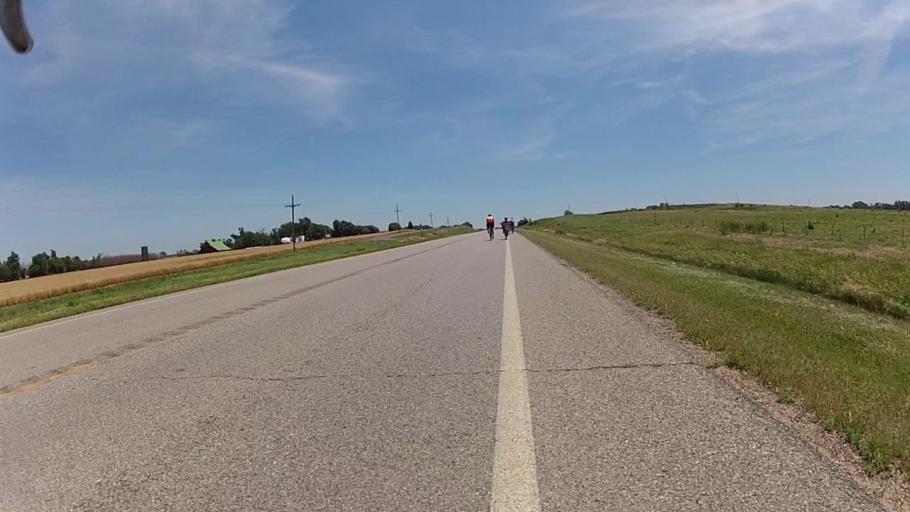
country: US
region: Kansas
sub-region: Barber County
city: Medicine Lodge
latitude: 37.2537
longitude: -98.4807
